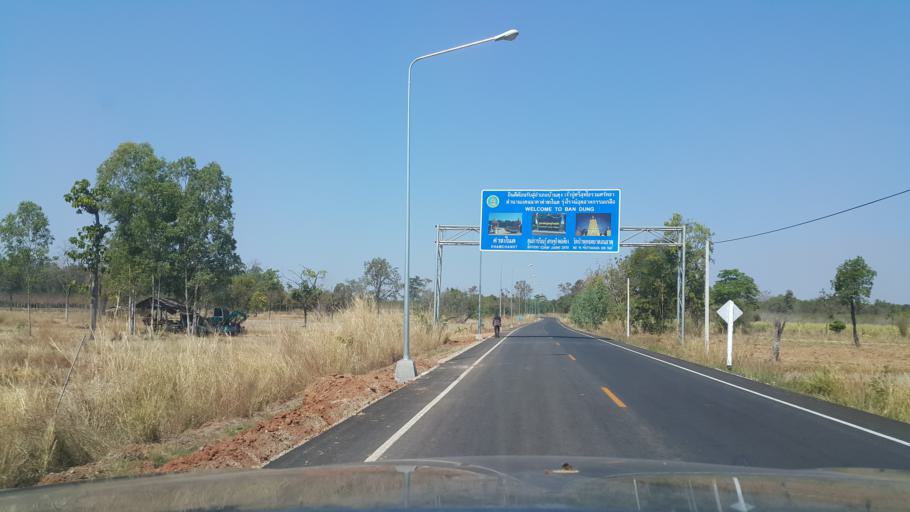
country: TH
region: Changwat Udon Thani
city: Ban Dung
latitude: 17.6102
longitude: 103.3150
